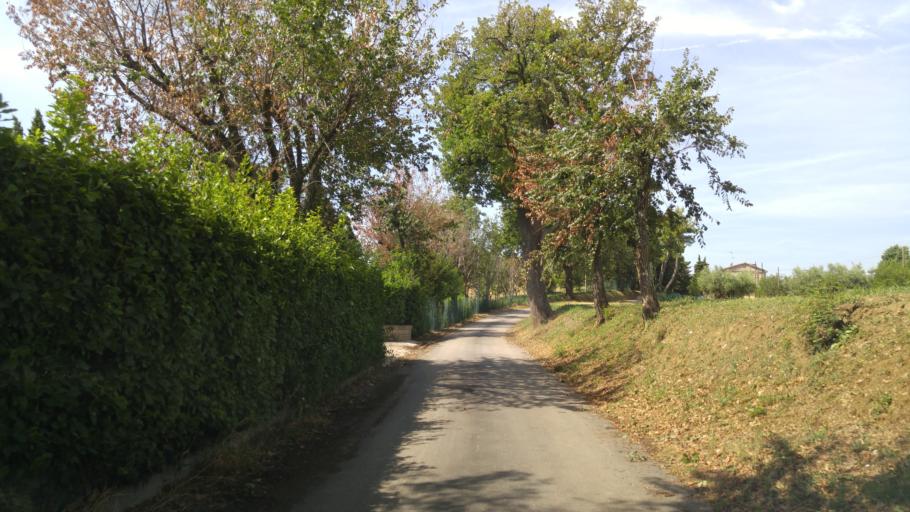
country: IT
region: The Marches
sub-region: Provincia di Pesaro e Urbino
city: Centinarola
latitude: 43.8479
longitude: 12.9852
